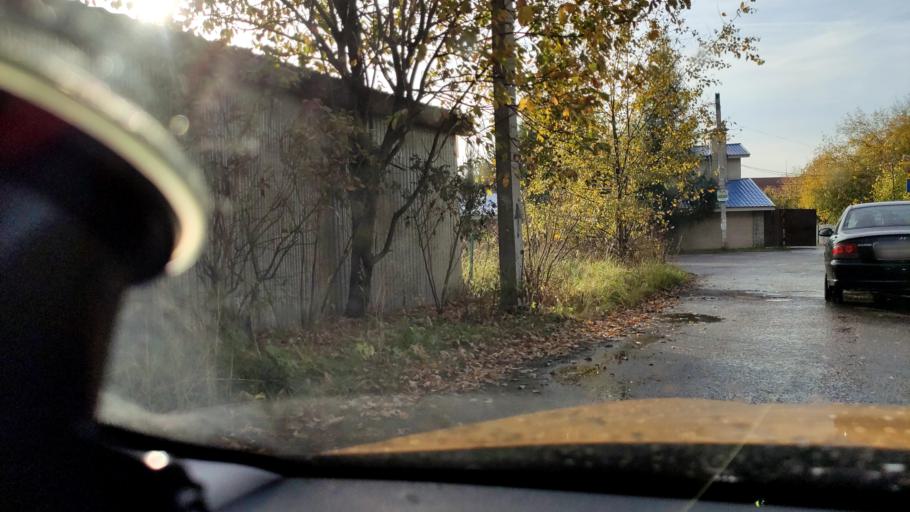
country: RU
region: Moskovskaya
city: Povedniki
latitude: 55.9383
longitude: 37.6544
